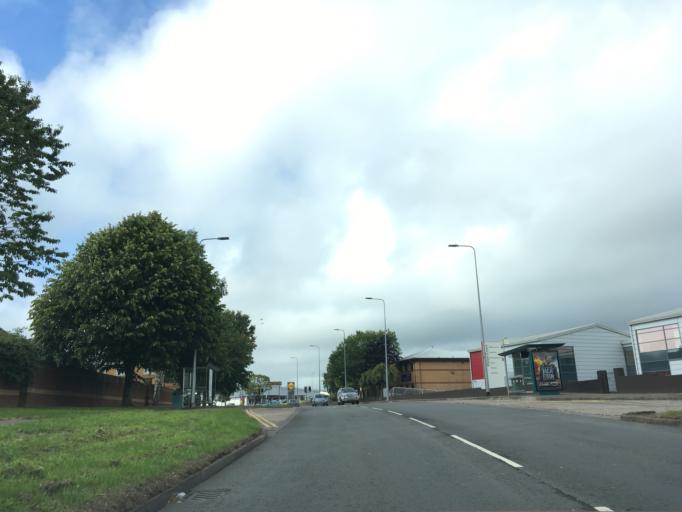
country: GB
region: Wales
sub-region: Newport
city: Marshfield
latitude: 51.5276
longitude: -3.1363
